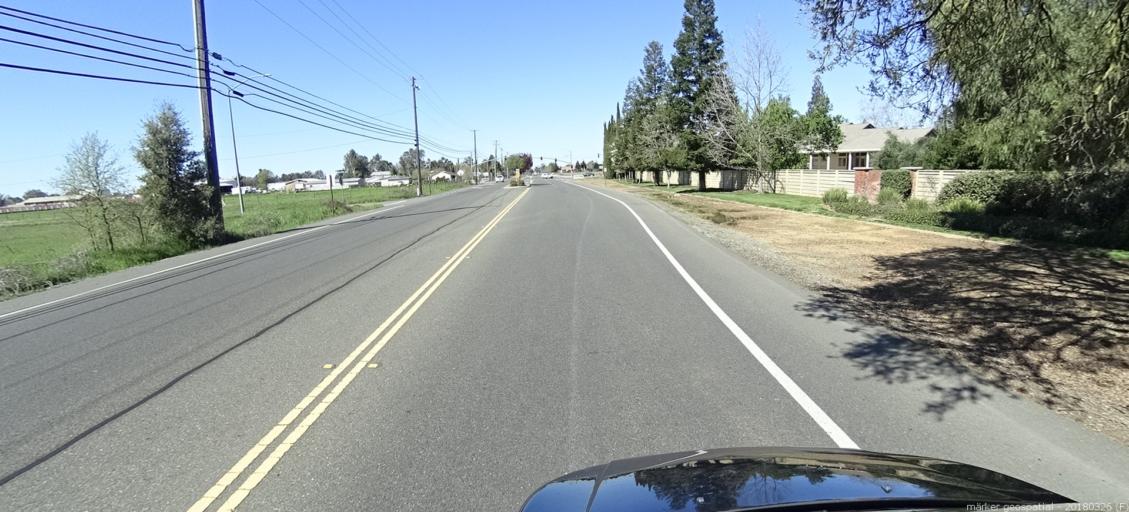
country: US
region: California
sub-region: Sacramento County
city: Vineyard
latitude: 38.4527
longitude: -121.3139
